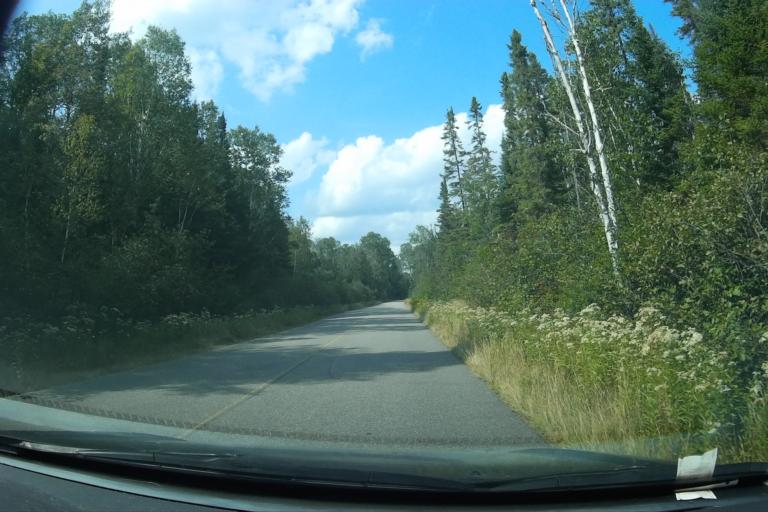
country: CA
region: Ontario
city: Bancroft
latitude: 45.6240
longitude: -78.3494
